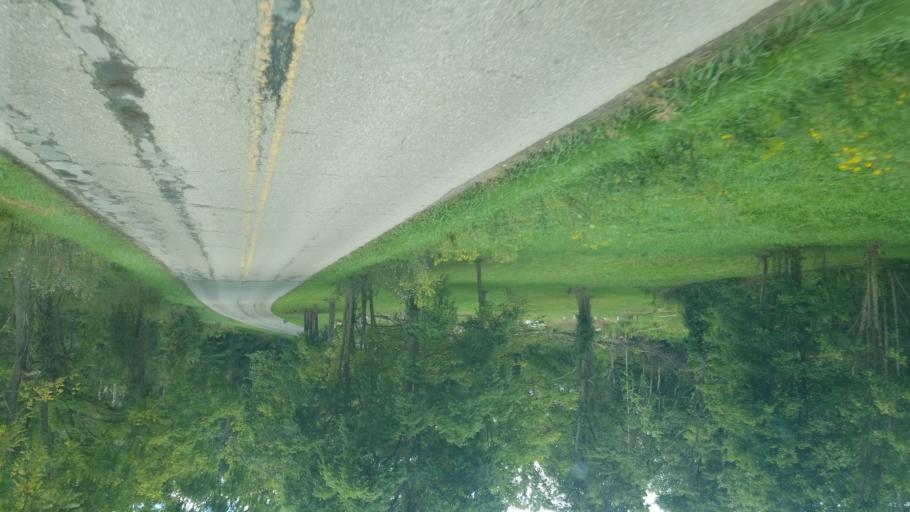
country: US
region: Ohio
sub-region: Jackson County
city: Oak Hill
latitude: 38.9449
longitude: -82.6167
